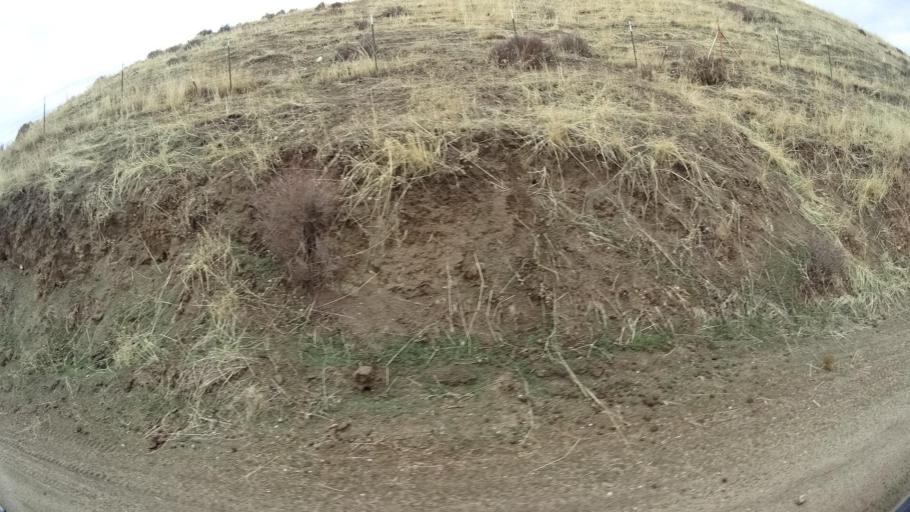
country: US
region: California
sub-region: Kern County
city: Stallion Springs
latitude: 35.1234
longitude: -118.7358
